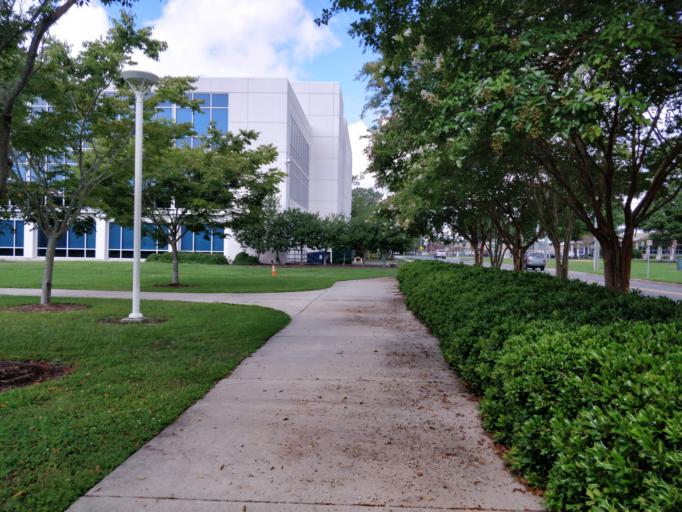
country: US
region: Virginia
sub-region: City of Chesapeake
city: Chesapeake
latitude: 36.7176
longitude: -76.2495
